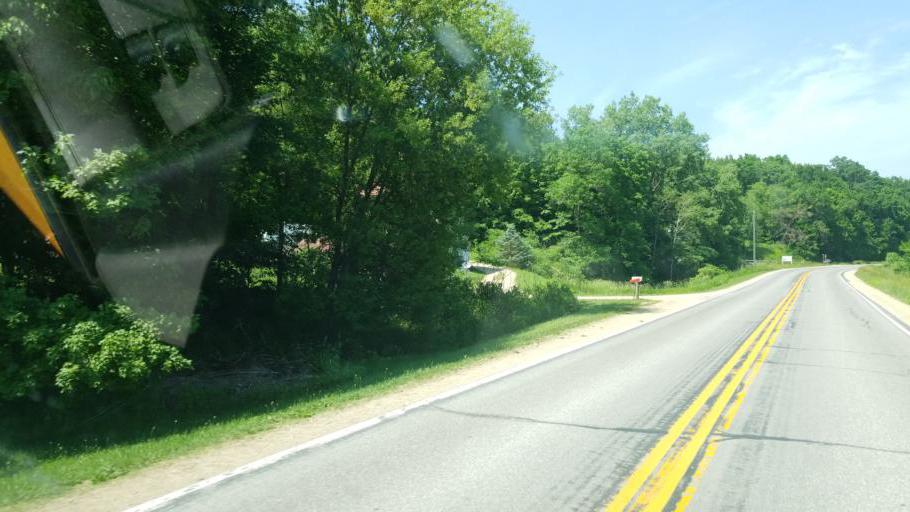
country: US
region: Wisconsin
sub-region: Vernon County
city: Hillsboro
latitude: 43.6410
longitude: -90.4402
